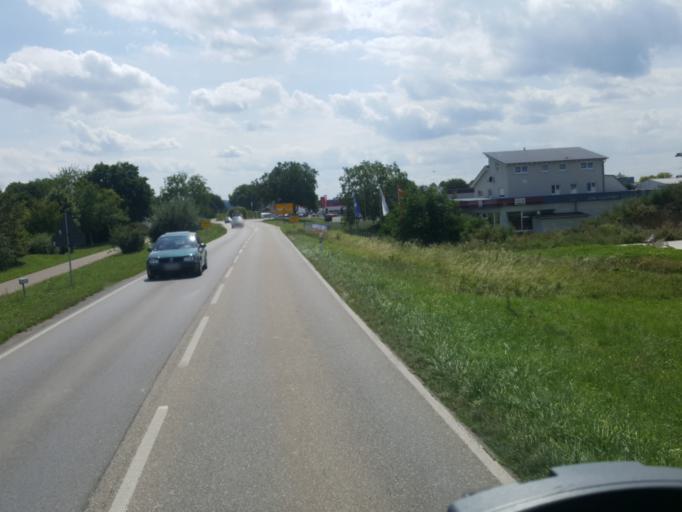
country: DE
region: Baden-Wuerttemberg
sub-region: Freiburg Region
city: Auggen
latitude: 47.7934
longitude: 7.5934
